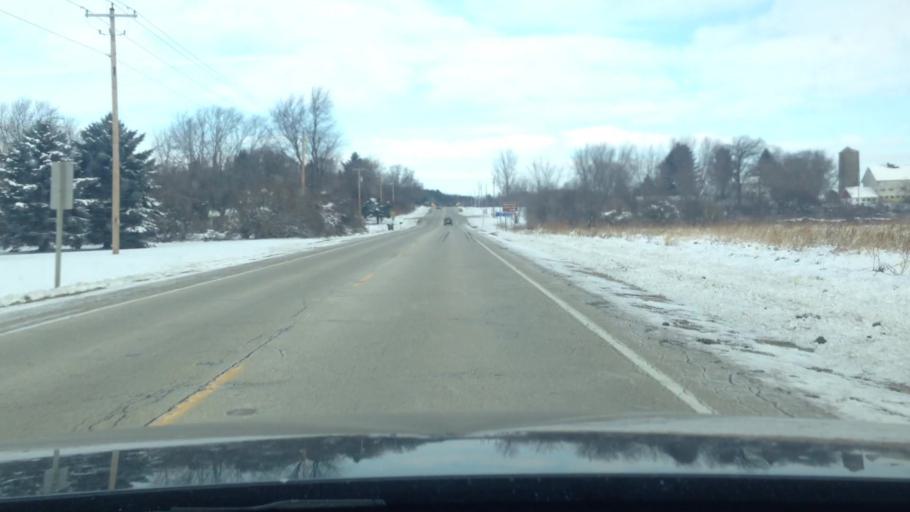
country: US
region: Wisconsin
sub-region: Walworth County
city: Lake Geneva
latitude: 42.6232
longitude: -88.4137
